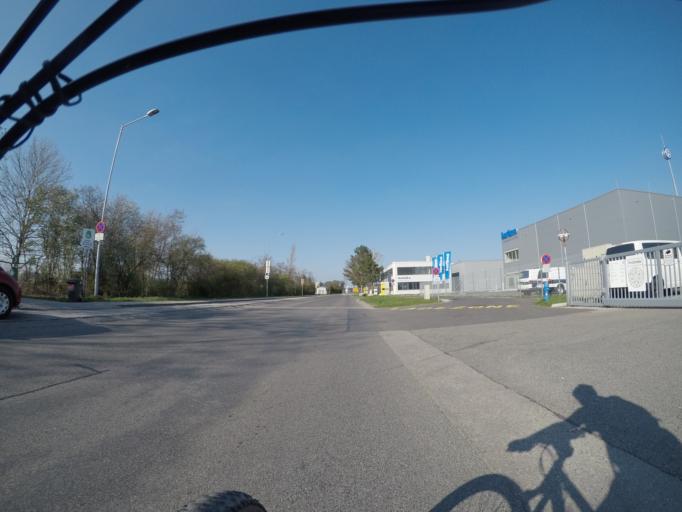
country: AT
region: Lower Austria
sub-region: Politischer Bezirk Modling
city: Wiener Neudorf
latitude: 48.0746
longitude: 16.3164
